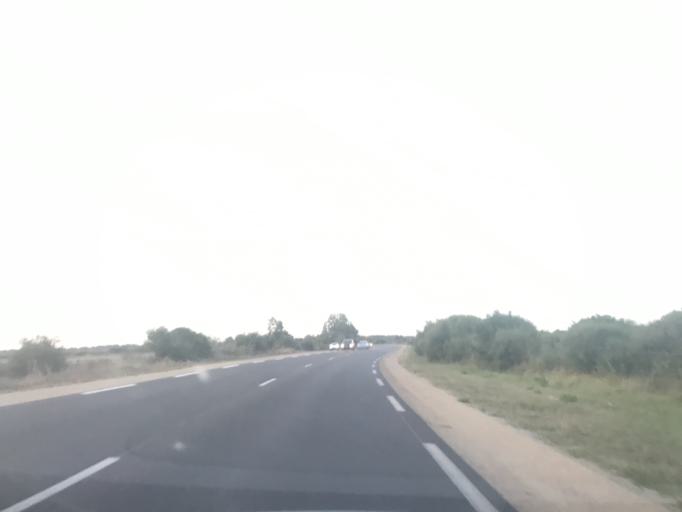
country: FR
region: Provence-Alpes-Cote d'Azur
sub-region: Departement des Bouches-du-Rhone
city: Saintes-Maries-de-la-Mer
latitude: 43.5386
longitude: 4.4007
